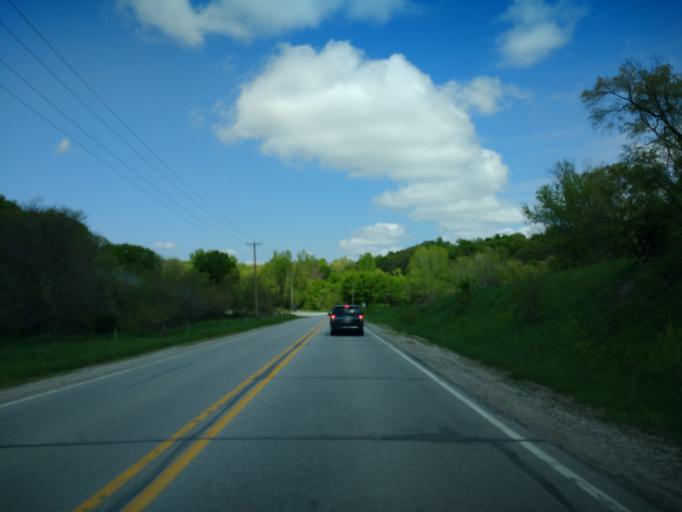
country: US
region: Iowa
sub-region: Harrison County
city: Missouri Valley
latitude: 41.4309
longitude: -95.8584
